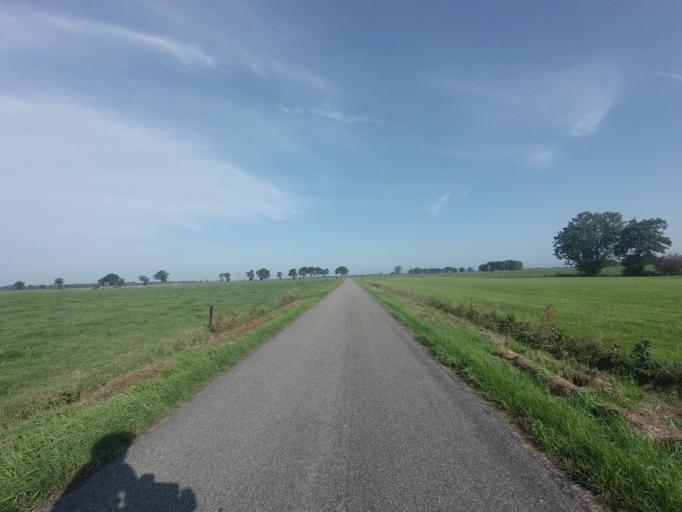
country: NL
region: Groningen
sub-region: Gemeente Leek
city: Leek
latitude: 53.1599
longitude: 6.4319
